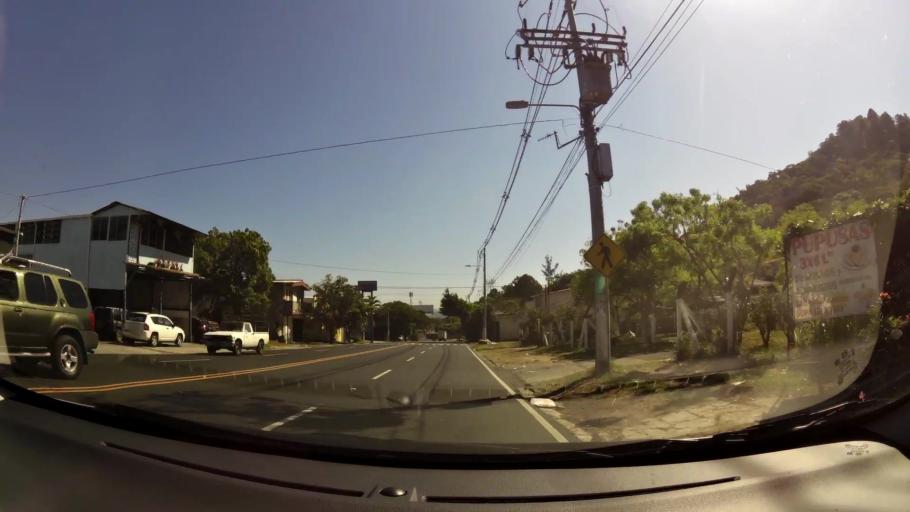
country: SV
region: La Libertad
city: Santa Tecla
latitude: 13.6666
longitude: -89.2870
